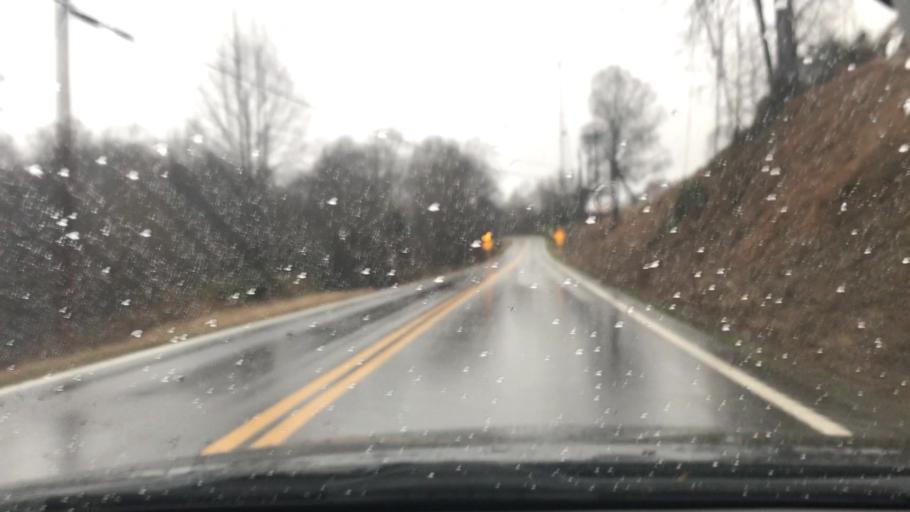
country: US
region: Tennessee
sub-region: Cheatham County
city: Ashland City
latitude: 36.2768
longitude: -87.1230
